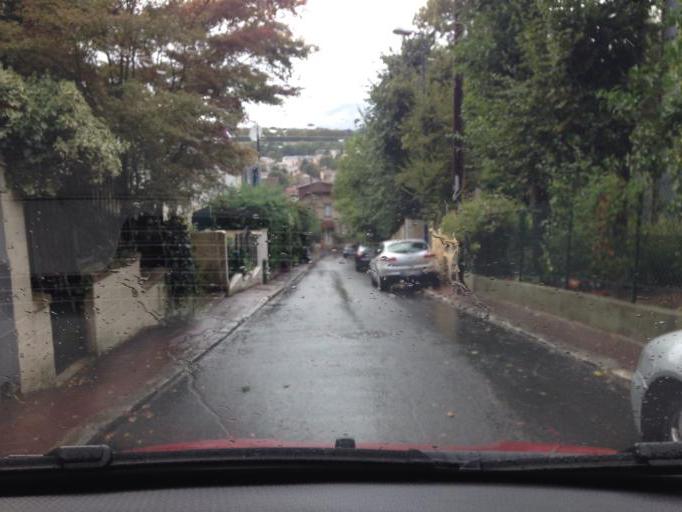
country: FR
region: Ile-de-France
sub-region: Departement des Hauts-de-Seine
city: Meudon
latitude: 48.8029
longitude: 2.2442
